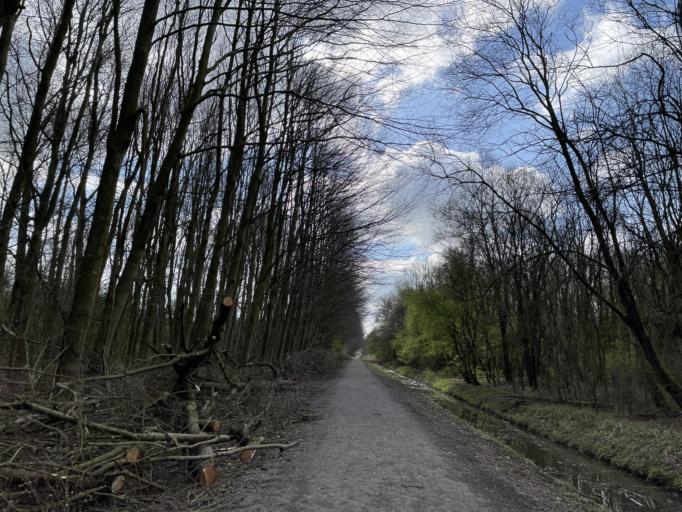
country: NL
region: South Holland
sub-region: Gemeente Pijnacker-Nootdorp
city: Pijnacker
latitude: 52.0451
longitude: 4.4532
